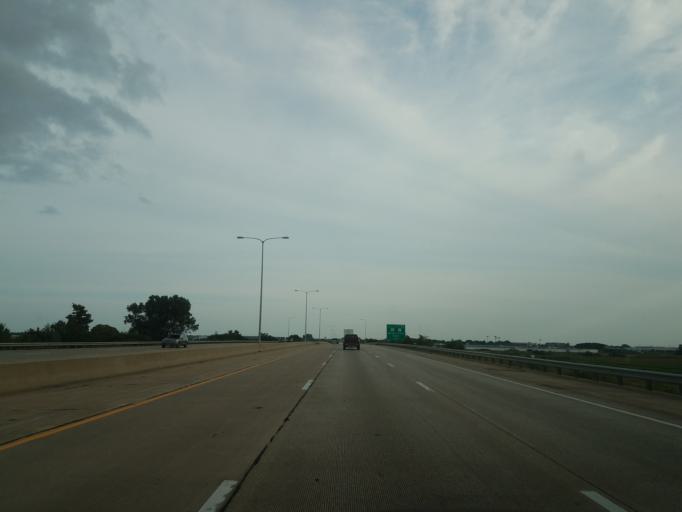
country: US
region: Illinois
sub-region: McLean County
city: Normal
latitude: 40.5063
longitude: -89.0289
